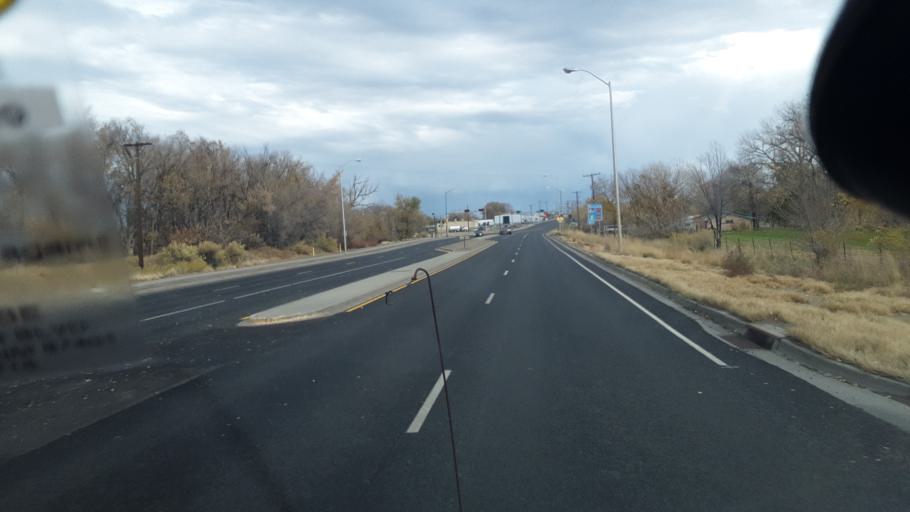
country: US
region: New Mexico
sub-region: San Juan County
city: Farmington
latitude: 36.7192
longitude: -108.2051
